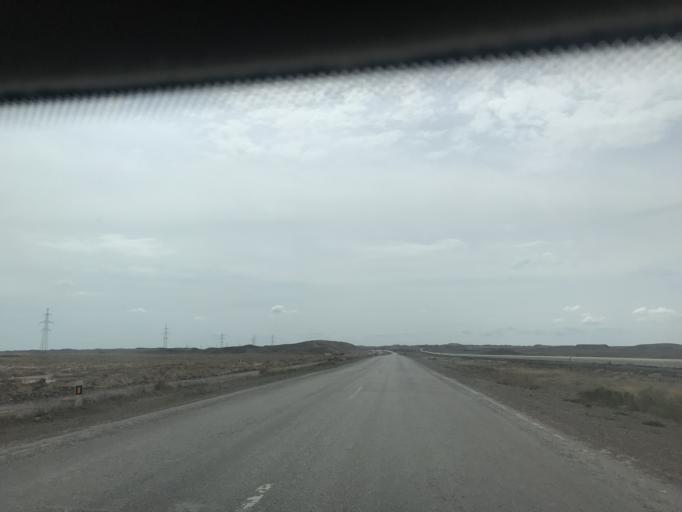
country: KZ
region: Zhambyl
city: Mynaral
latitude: 45.3807
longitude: 73.6524
